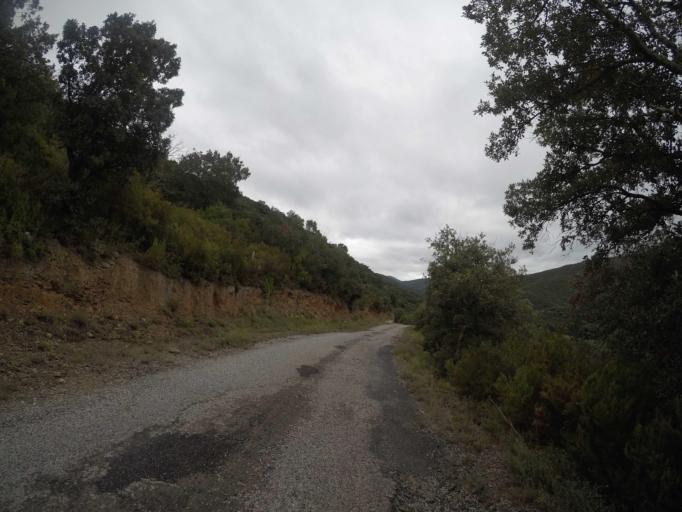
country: FR
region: Languedoc-Roussillon
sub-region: Departement des Pyrenees-Orientales
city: Ille-sur-Tet
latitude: 42.6140
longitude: 2.6050
